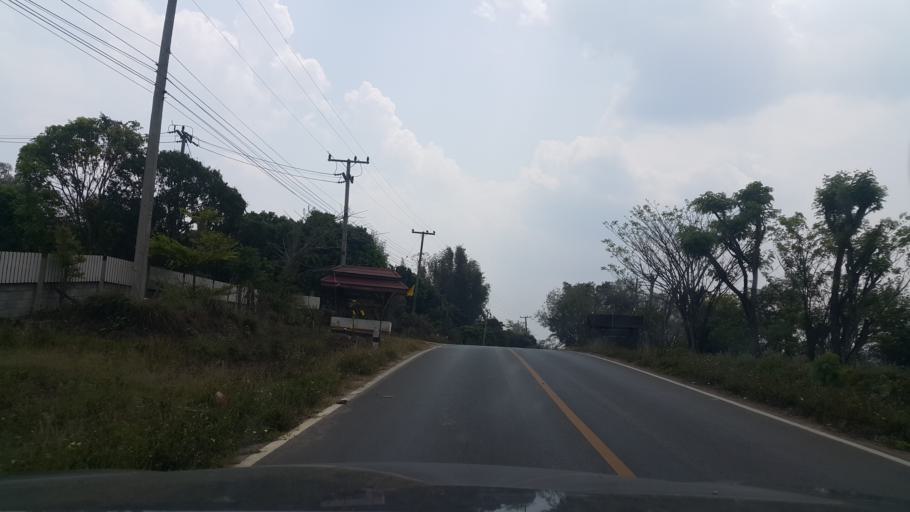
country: TH
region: Lamphun
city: Thung Hua Chang
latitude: 18.1294
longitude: 99.0129
